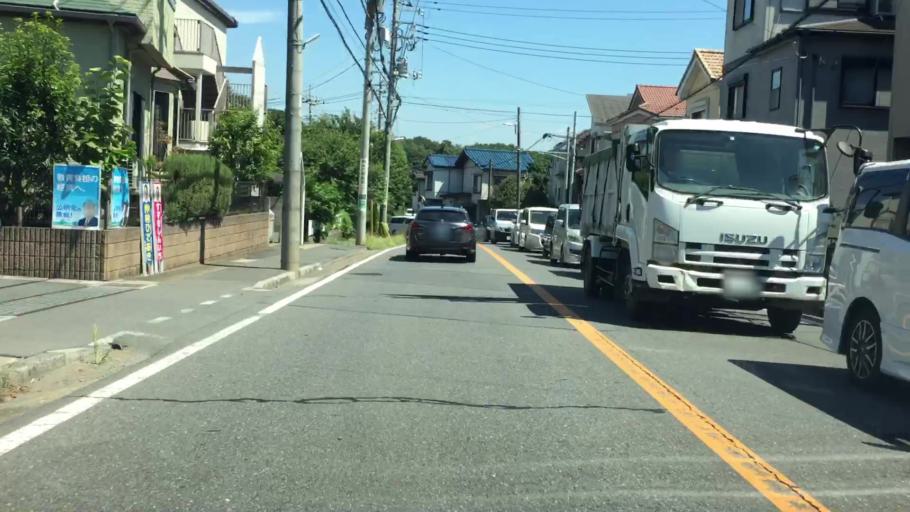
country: JP
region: Chiba
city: Funabashi
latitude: 35.7264
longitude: 139.9956
